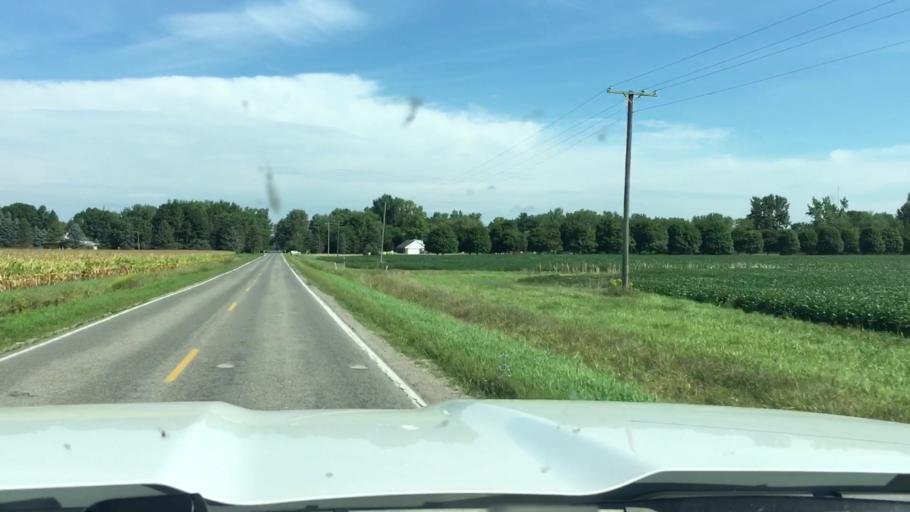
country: US
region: Michigan
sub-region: Saginaw County
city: Hemlock
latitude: 43.4681
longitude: -84.2303
